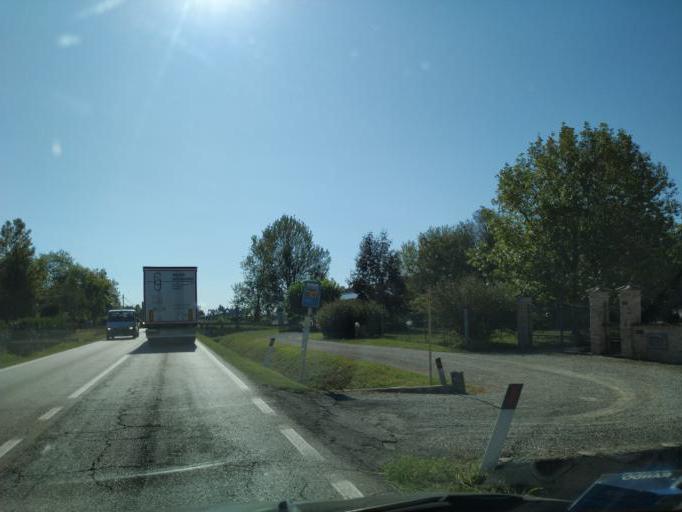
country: IT
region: Emilia-Romagna
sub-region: Provincia di Bologna
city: Sant'Agata Bolognese
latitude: 44.6551
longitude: 11.1404
